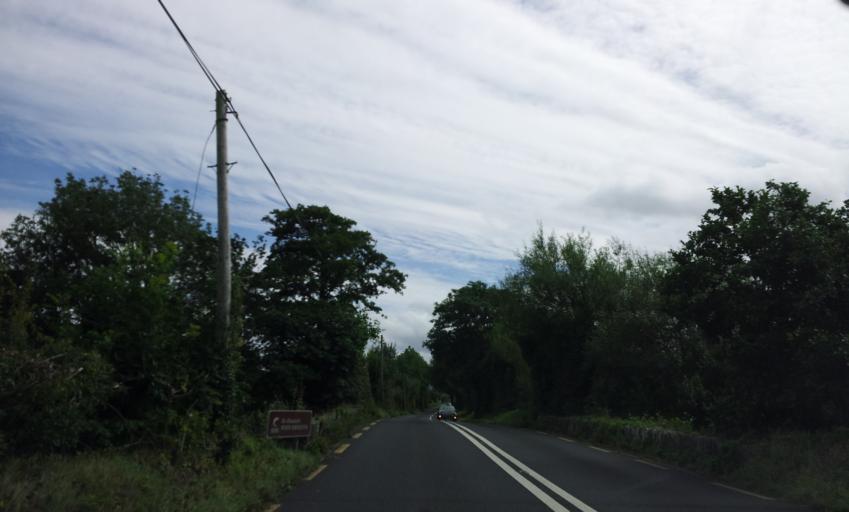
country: IE
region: Munster
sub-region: Ciarrai
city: Killorglin
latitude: 52.0953
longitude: -9.6968
